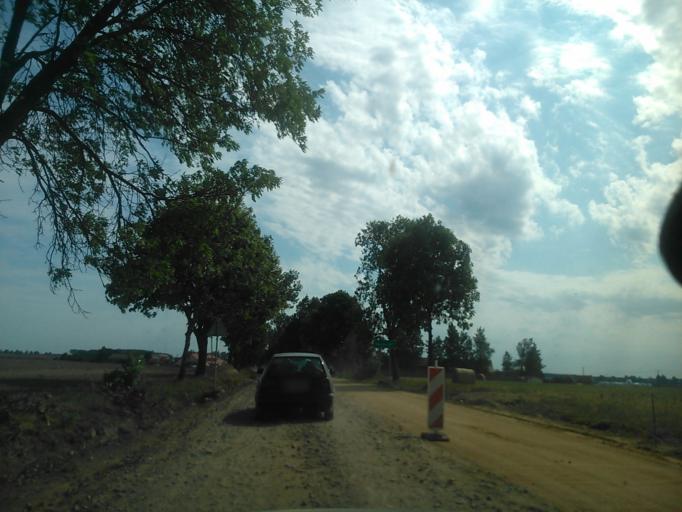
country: PL
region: Warmian-Masurian Voivodeship
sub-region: Powiat dzialdowski
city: Ilowo -Osada
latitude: 53.2027
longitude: 20.2424
